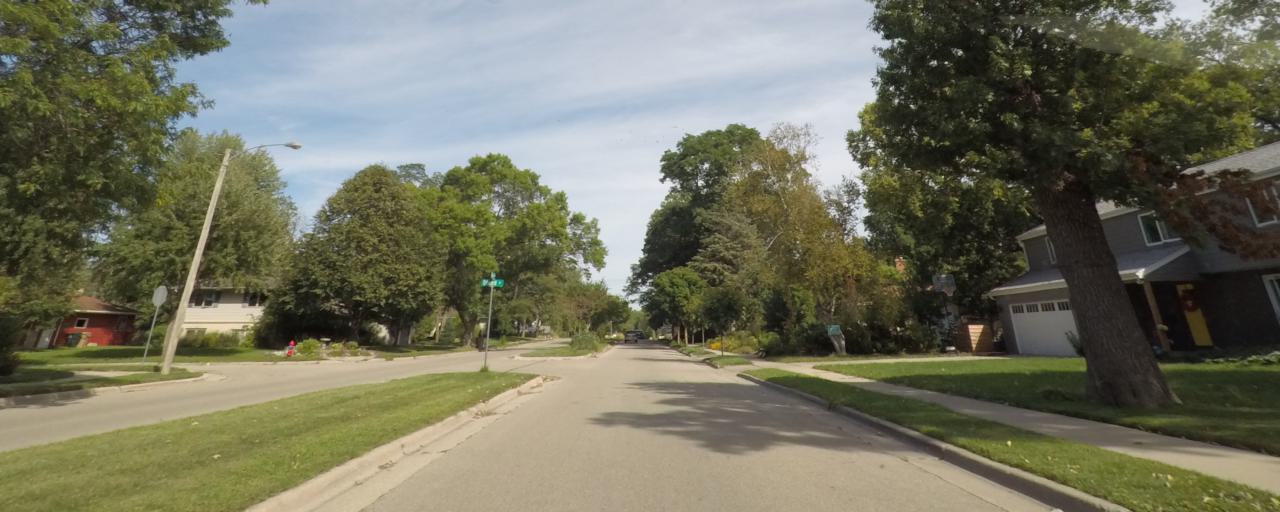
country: US
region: Wisconsin
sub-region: Dane County
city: Shorewood Hills
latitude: 43.0536
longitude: -89.4604
